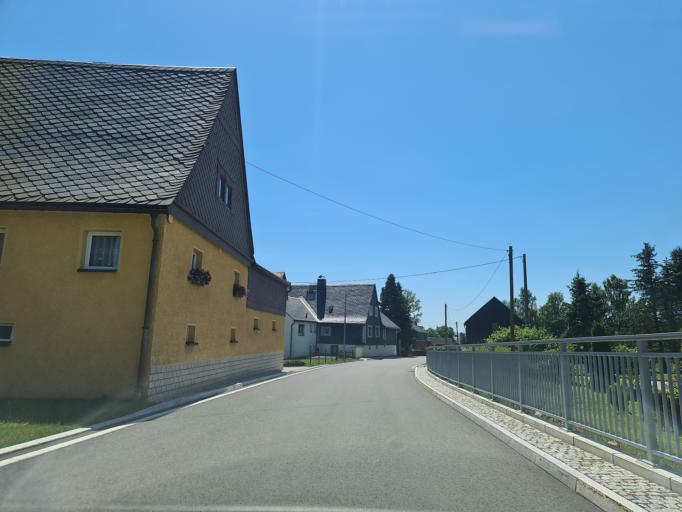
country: DE
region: Saxony
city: Rechenberg-Bienenmuhle
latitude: 50.7140
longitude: 13.5120
